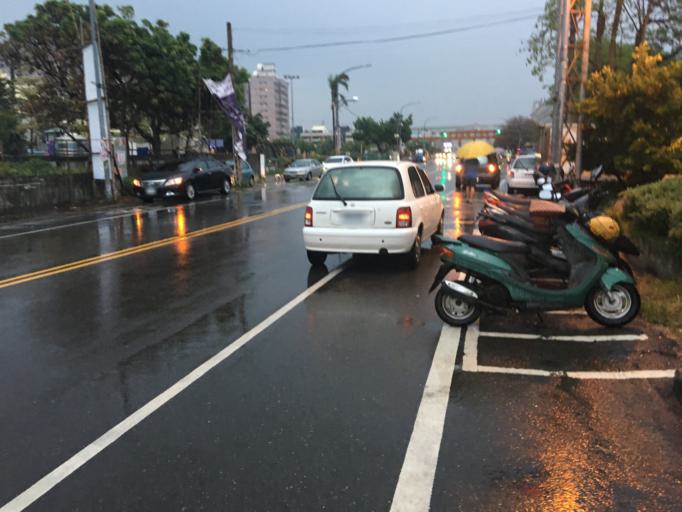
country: TW
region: Taiwan
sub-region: Changhua
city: Chang-hua
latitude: 24.0867
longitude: 120.5486
